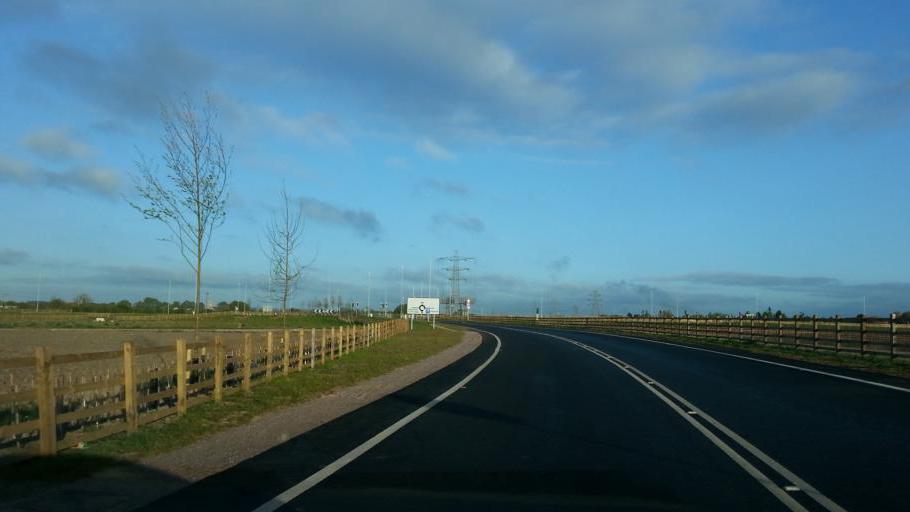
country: GB
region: England
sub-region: Nottinghamshire
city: Newark on Trent
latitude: 53.0523
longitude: -0.8030
